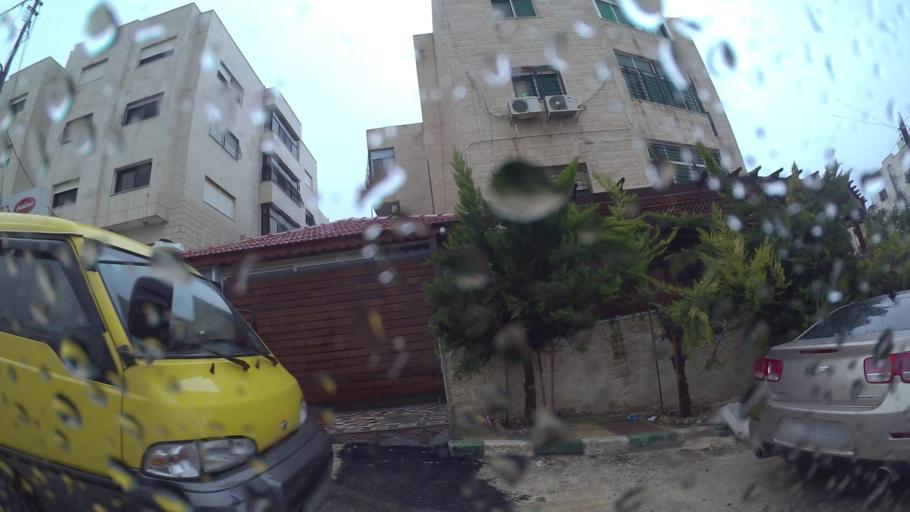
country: JO
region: Amman
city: Al Jubayhah
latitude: 32.0292
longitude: 35.8500
